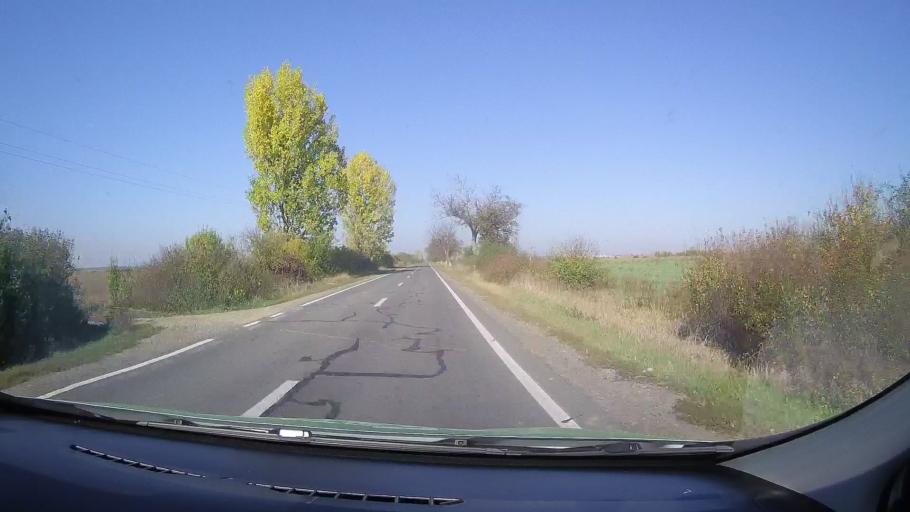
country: RO
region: Satu Mare
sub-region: Comuna Urziceni
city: Urziceni
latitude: 47.7117
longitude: 22.4262
